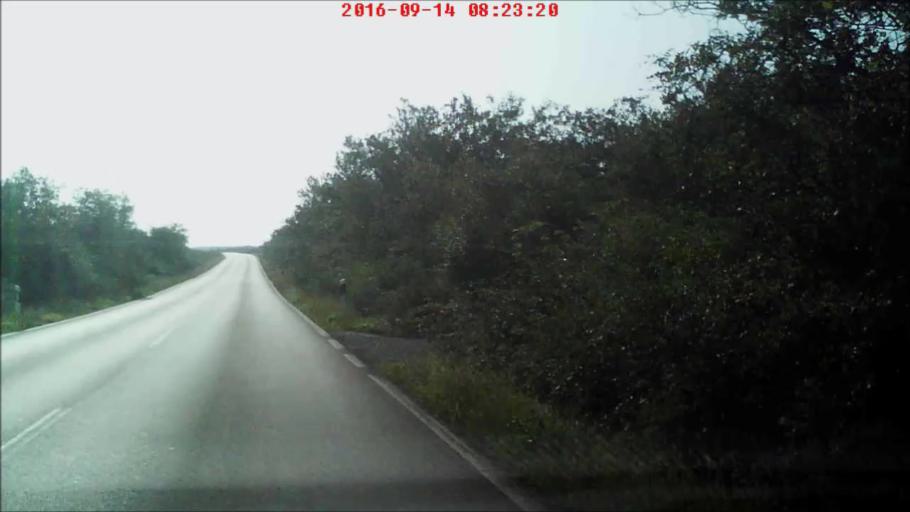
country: HR
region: Zadarska
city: Nin
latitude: 44.2130
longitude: 15.2296
